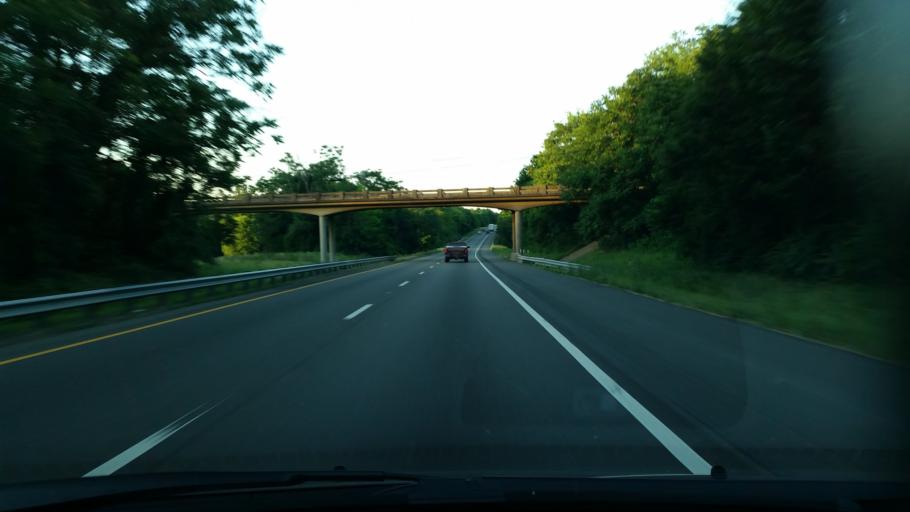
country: US
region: Tennessee
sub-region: Jefferson County
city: White Pine
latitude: 36.1172
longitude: -83.3278
